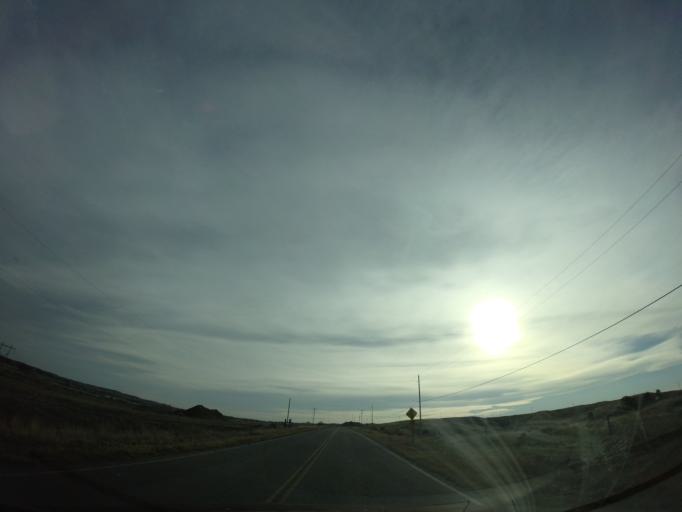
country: US
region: Montana
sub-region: Yellowstone County
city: Billings
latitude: 45.7908
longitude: -108.4555
